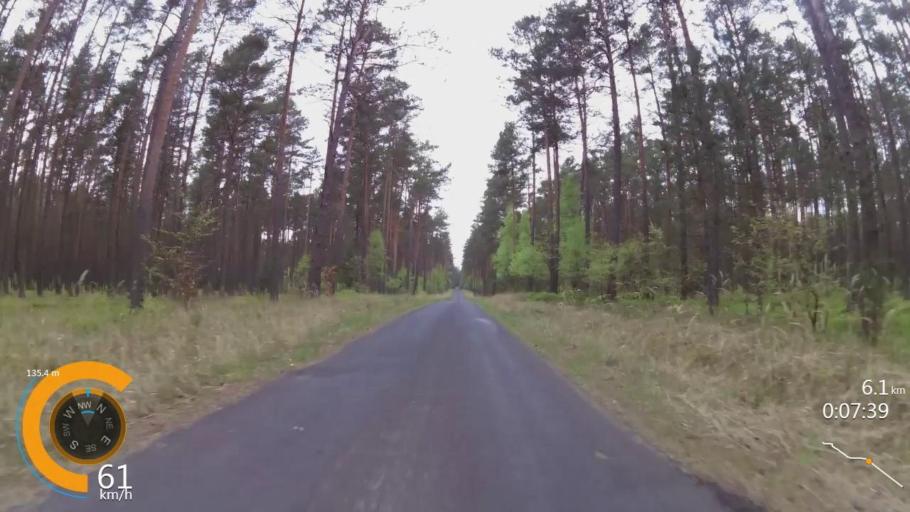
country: PL
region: West Pomeranian Voivodeship
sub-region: Powiat drawski
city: Wierzchowo
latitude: 53.4985
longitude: 16.1597
